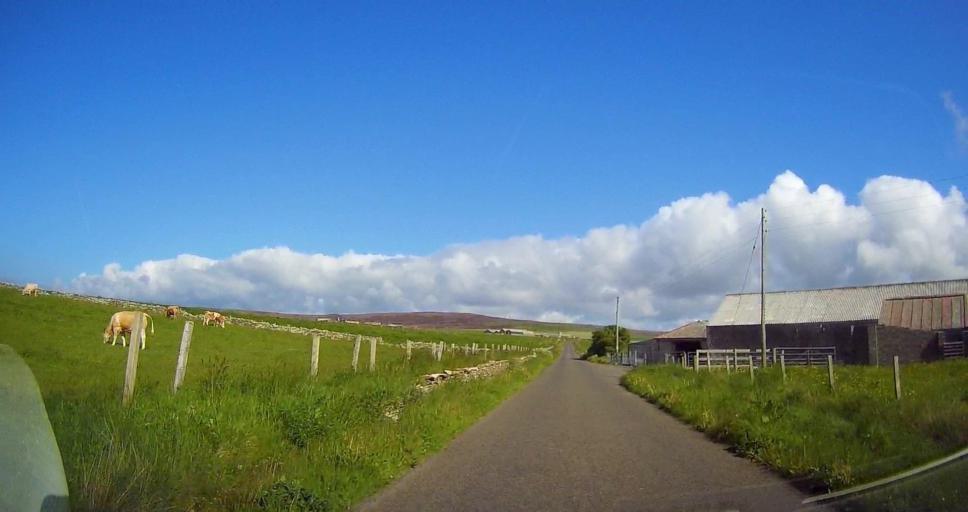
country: GB
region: Scotland
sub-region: Orkney Islands
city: Stromness
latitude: 58.9880
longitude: -3.1515
